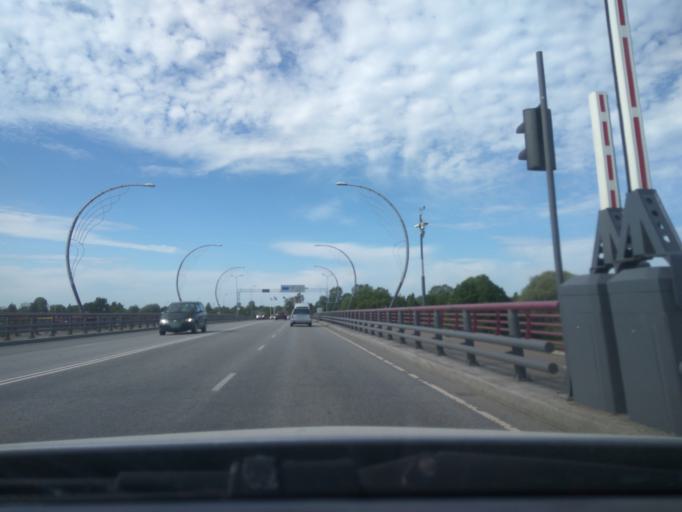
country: LV
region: Ventspils
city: Ventspils
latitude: 57.3885
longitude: 21.5884
